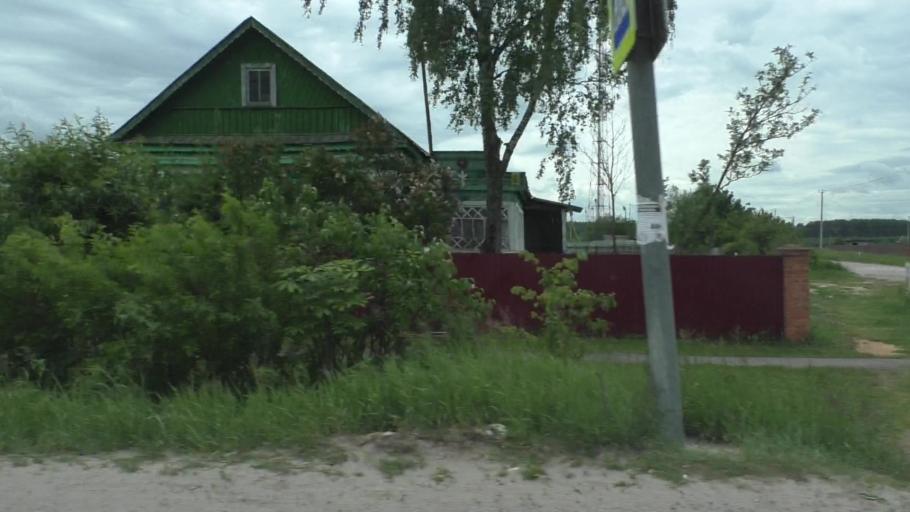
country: RU
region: Moskovskaya
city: Il'inskiy Pogost
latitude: 55.5037
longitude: 38.7842
